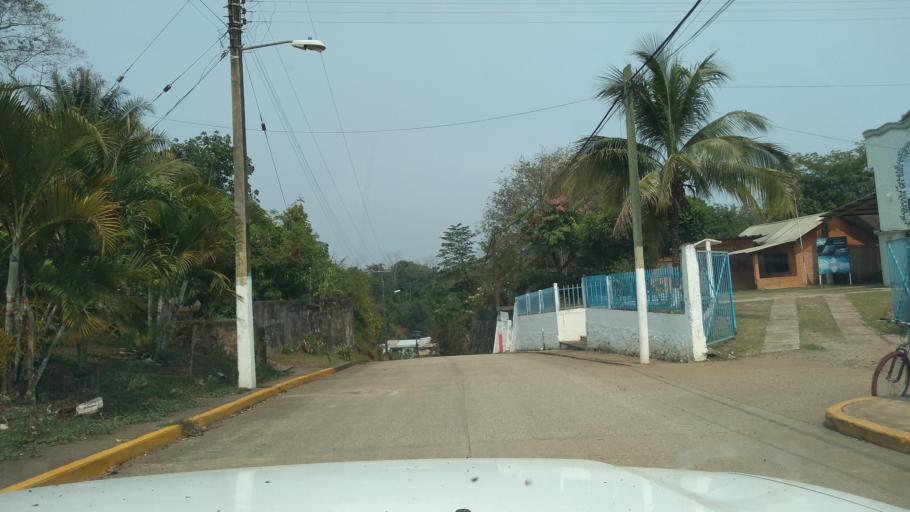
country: MX
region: Veracruz
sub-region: Tezonapa
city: Laguna Chica (Pueblo Nuevo)
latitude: 18.5311
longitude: -96.7901
